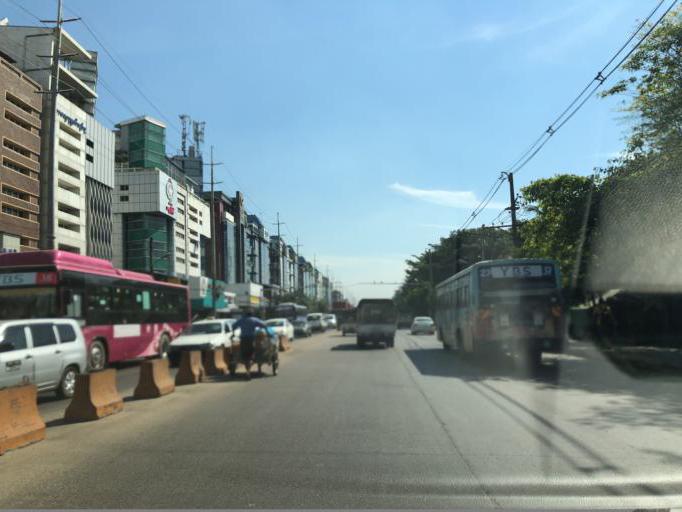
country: MM
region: Yangon
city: Yangon
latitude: 16.8321
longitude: 96.1211
